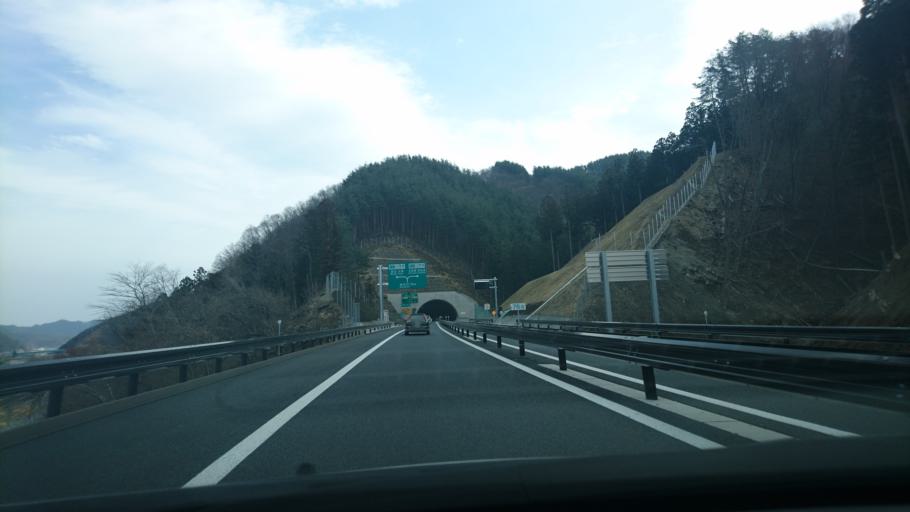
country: JP
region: Iwate
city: Kamaishi
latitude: 39.2545
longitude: 141.8216
